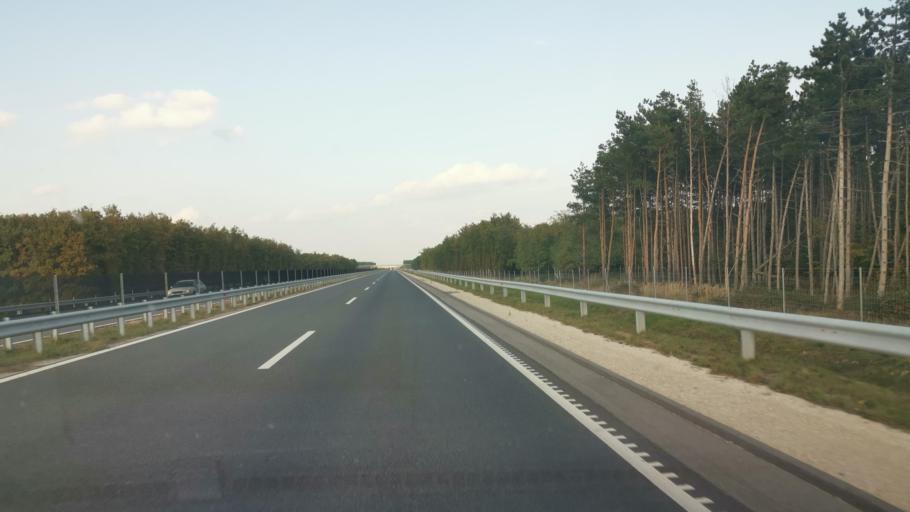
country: HU
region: Gyor-Moson-Sopron
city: Fertoszentmiklos
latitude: 47.5601
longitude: 16.8914
